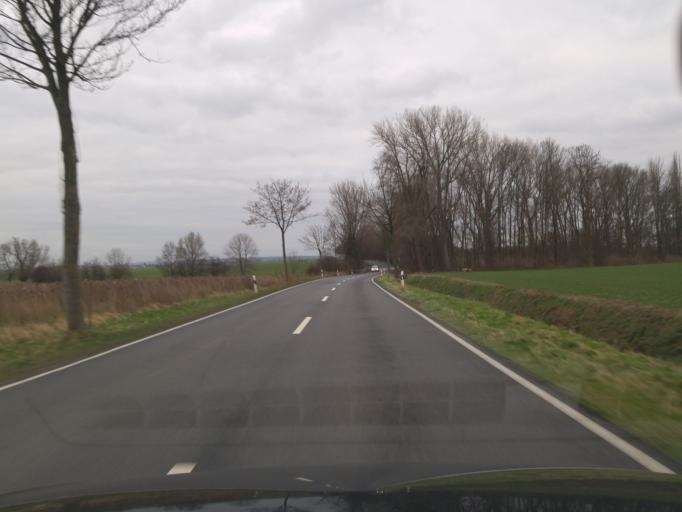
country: DE
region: Lower Saxony
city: Ilsede
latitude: 52.2334
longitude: 10.1723
